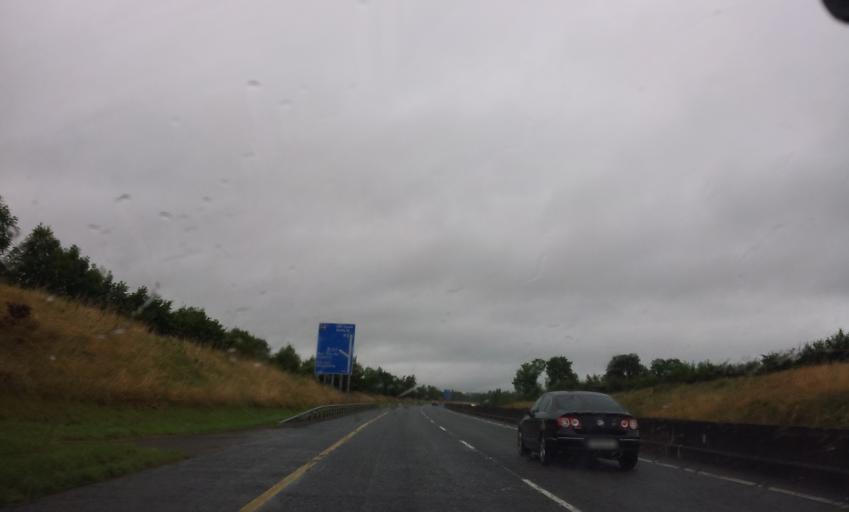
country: IE
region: Munster
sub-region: County Cork
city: Fermoy
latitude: 52.1469
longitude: -8.2656
